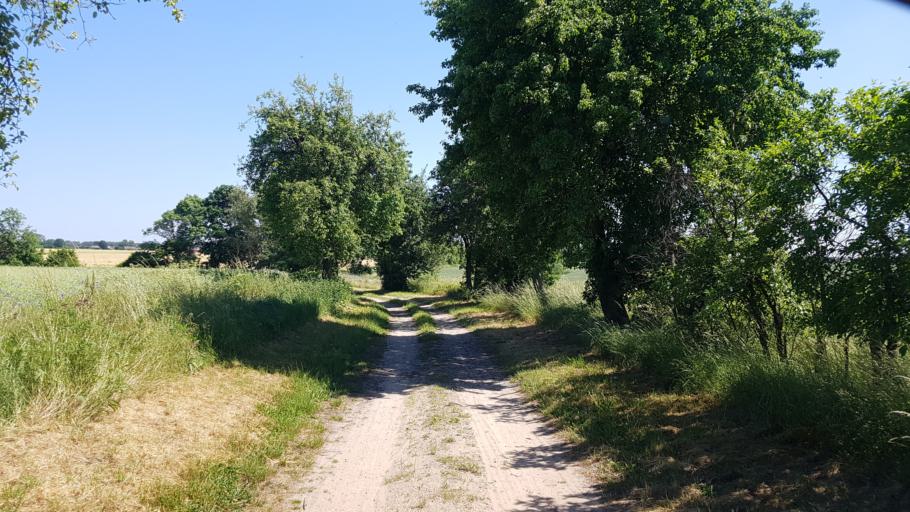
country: DE
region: Brandenburg
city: Sonnewalde
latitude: 51.7001
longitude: 13.6678
